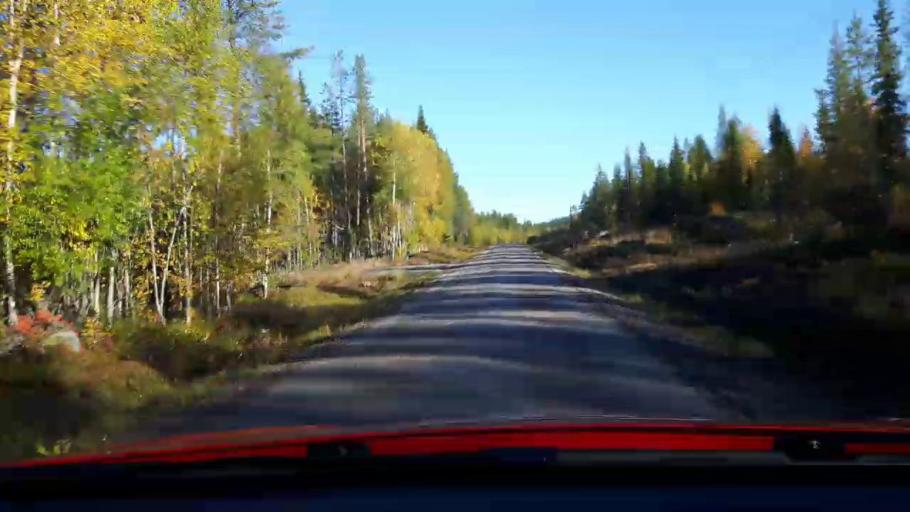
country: SE
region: Jaemtland
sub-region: Stroemsunds Kommun
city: Stroemsund
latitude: 64.3888
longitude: 15.1509
